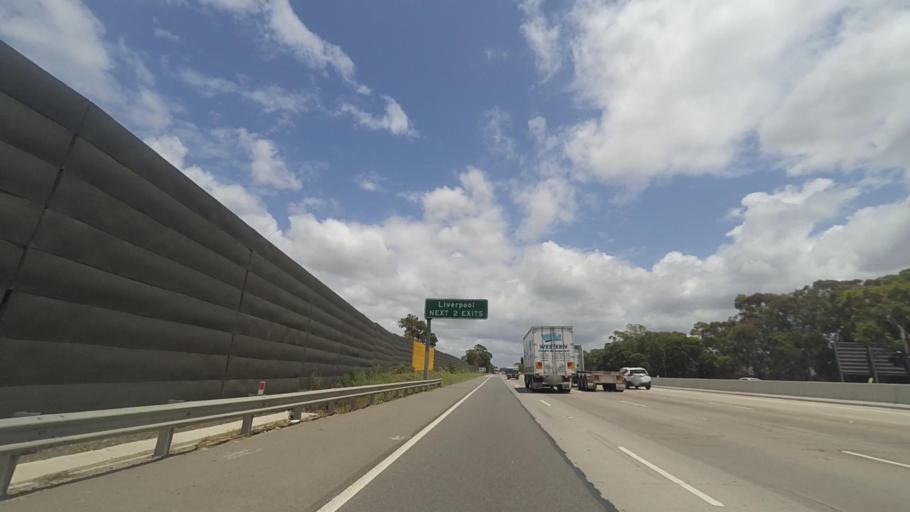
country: AU
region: New South Wales
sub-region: Fairfield
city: Liverpool
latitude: -33.9416
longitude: 150.9377
